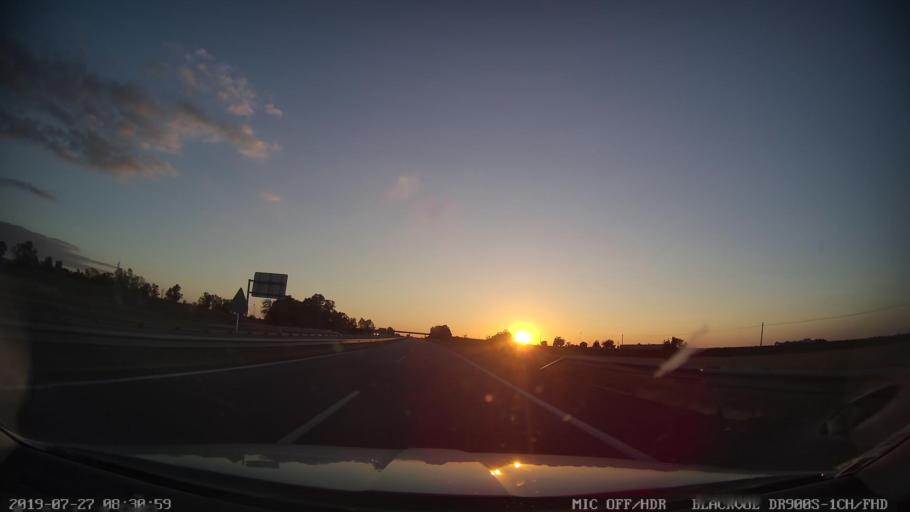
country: ES
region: Extremadura
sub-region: Provincia de Badajoz
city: Valdelacalzada
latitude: 38.8530
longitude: -6.7246
